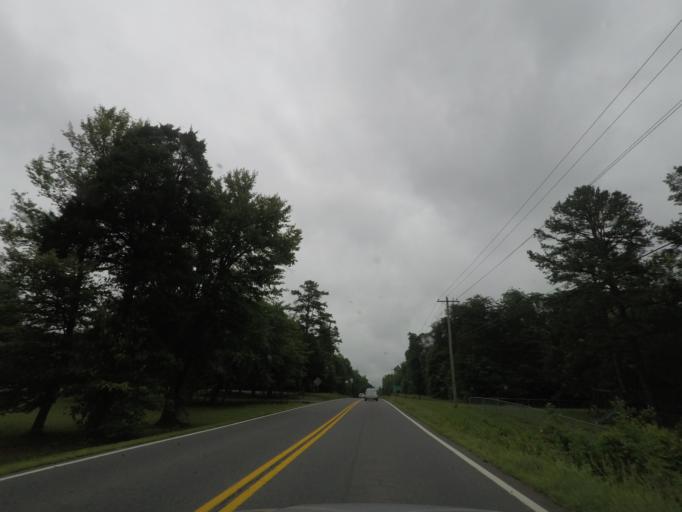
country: US
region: Virginia
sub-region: Fluvanna County
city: Palmyra
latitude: 37.9261
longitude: -78.2507
